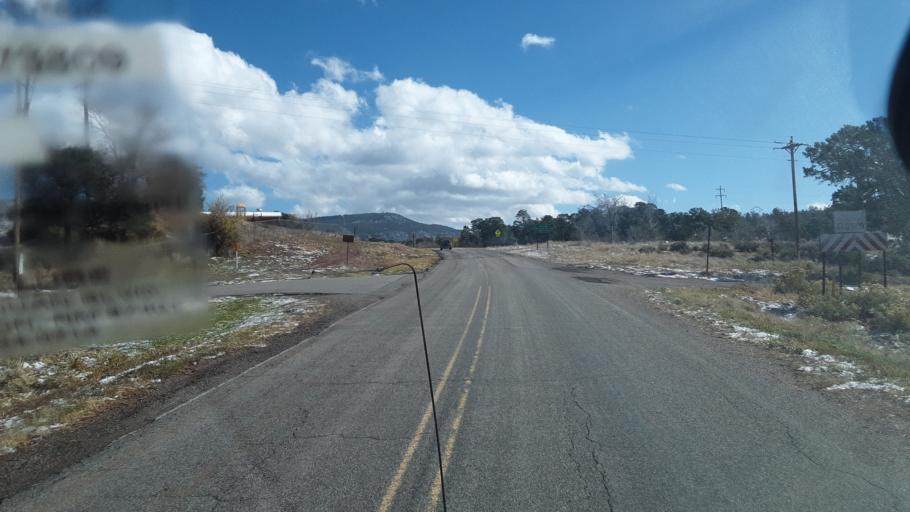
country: US
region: New Mexico
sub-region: Rio Arriba County
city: Santa Teresa
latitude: 36.2288
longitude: -106.8258
